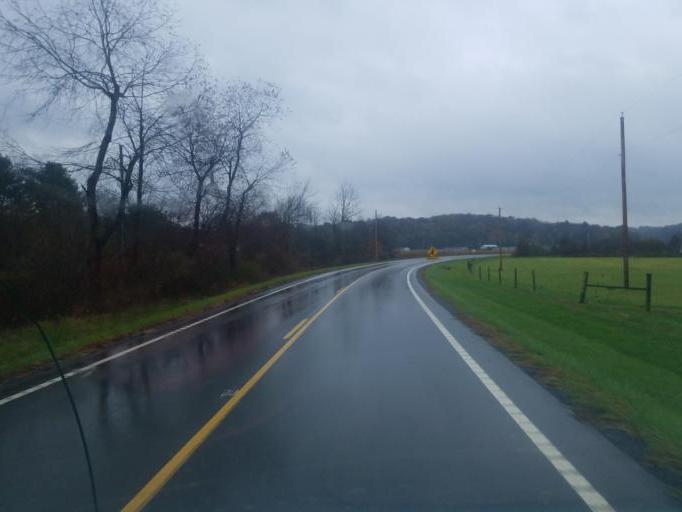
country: US
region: Ohio
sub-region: Muskingum County
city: Frazeysburg
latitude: 40.1355
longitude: -82.2008
